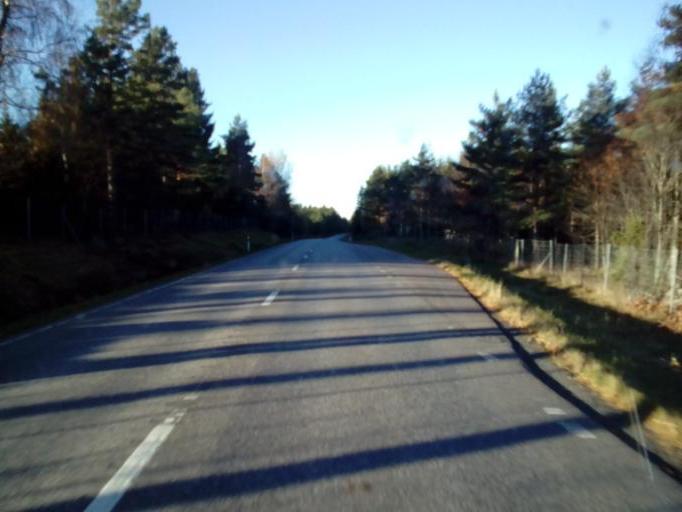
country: SE
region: OErebro
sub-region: Hallsbergs Kommun
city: Palsboda
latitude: 58.9277
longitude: 15.4307
